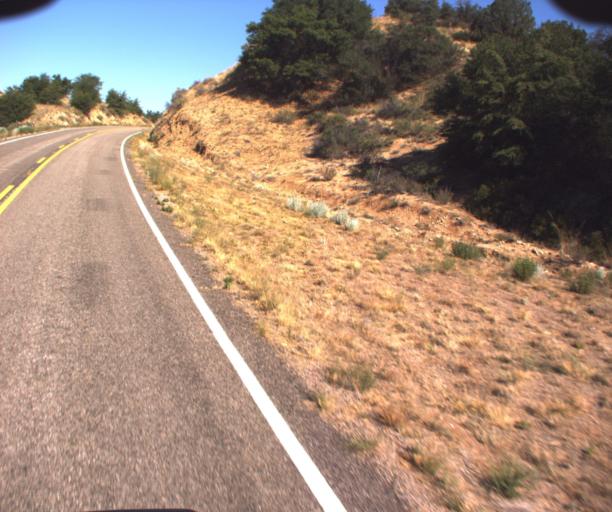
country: US
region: Arizona
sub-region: Graham County
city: Swift Trail Junction
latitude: 32.5774
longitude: -109.8471
